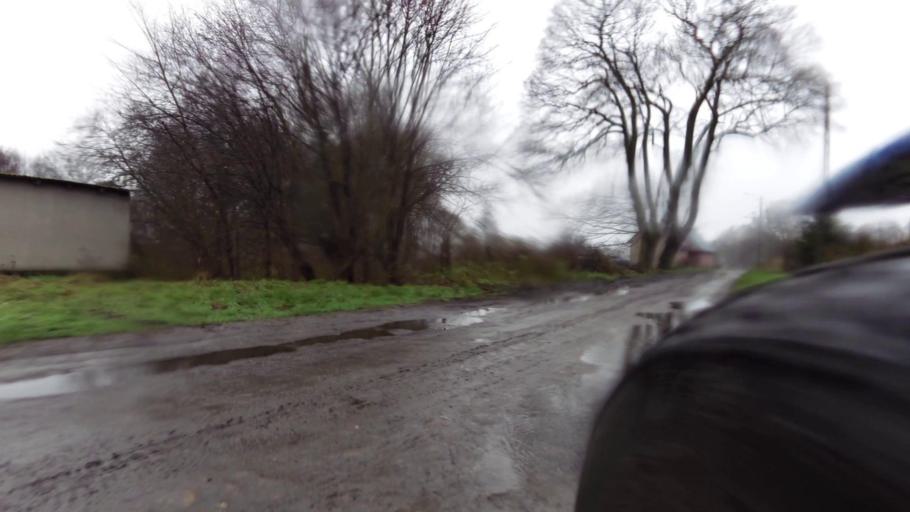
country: PL
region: West Pomeranian Voivodeship
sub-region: Powiat drawski
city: Zlocieniec
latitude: 53.5443
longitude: 15.9526
